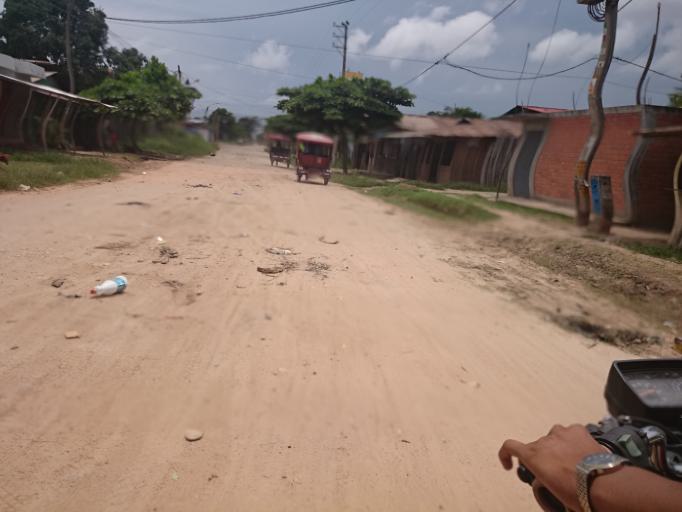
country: PE
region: Ucayali
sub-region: Provincia de Coronel Portillo
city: Pucallpa
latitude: -8.3763
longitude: -74.5592
